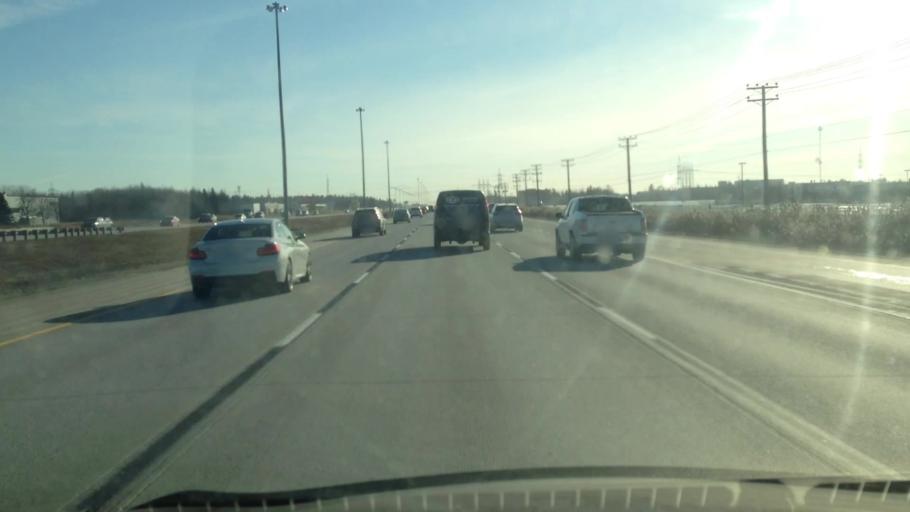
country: CA
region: Quebec
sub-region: Laurentides
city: Blainville
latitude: 45.6905
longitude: -73.9344
